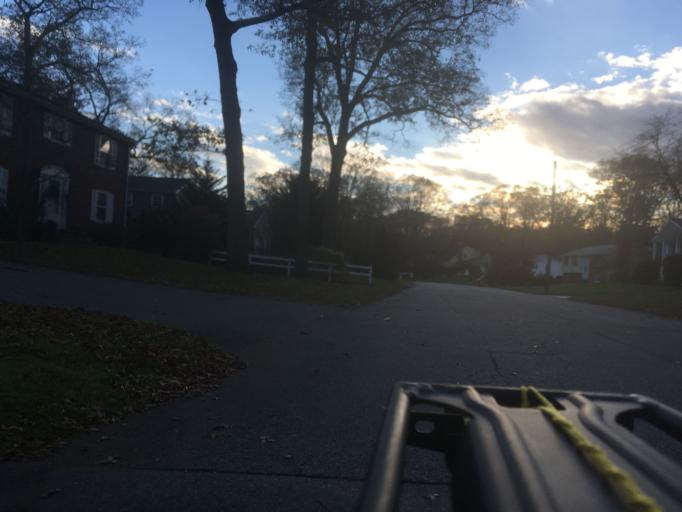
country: US
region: Rhode Island
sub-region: Kent County
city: East Greenwich
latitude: 41.6476
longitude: -71.4692
